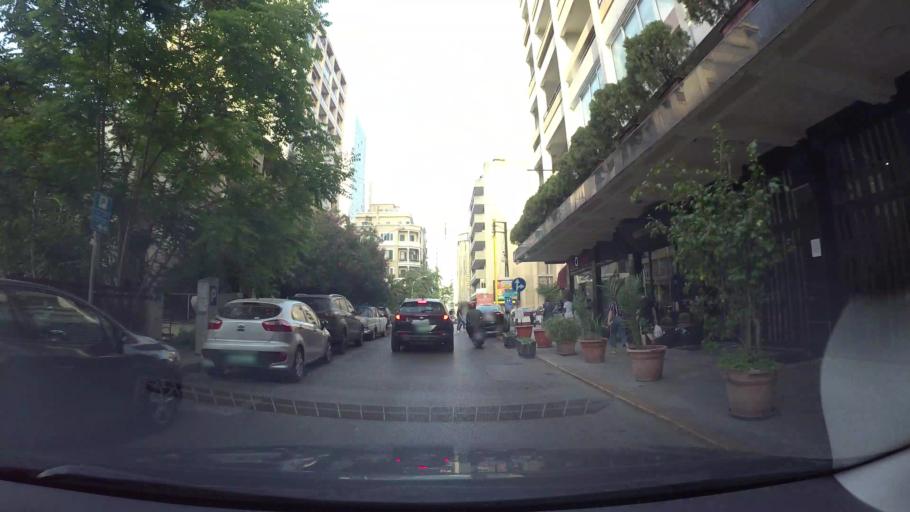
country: LB
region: Beyrouth
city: Ra's Bayrut
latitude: 33.8979
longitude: 35.4910
